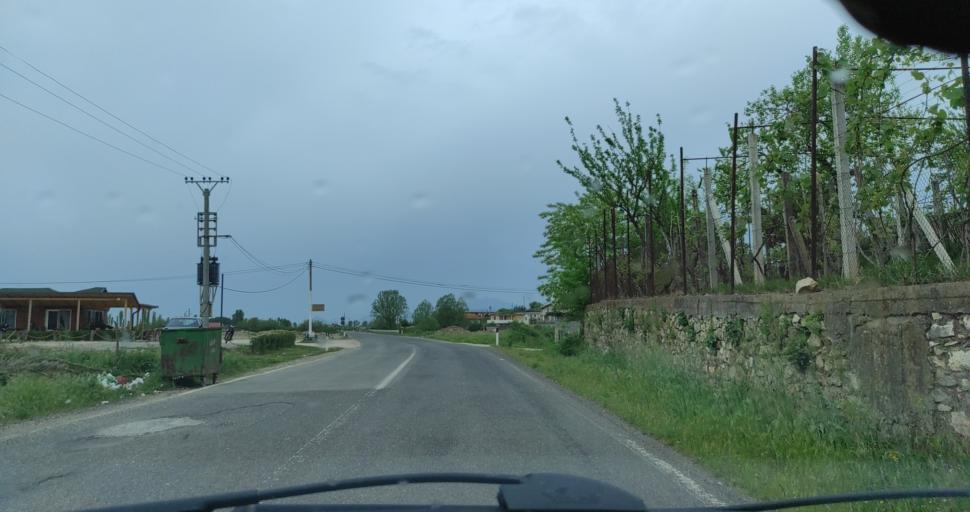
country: AL
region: Lezhe
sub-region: Rrethi i Kurbinit
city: Mamurras
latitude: 41.5921
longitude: 19.6990
